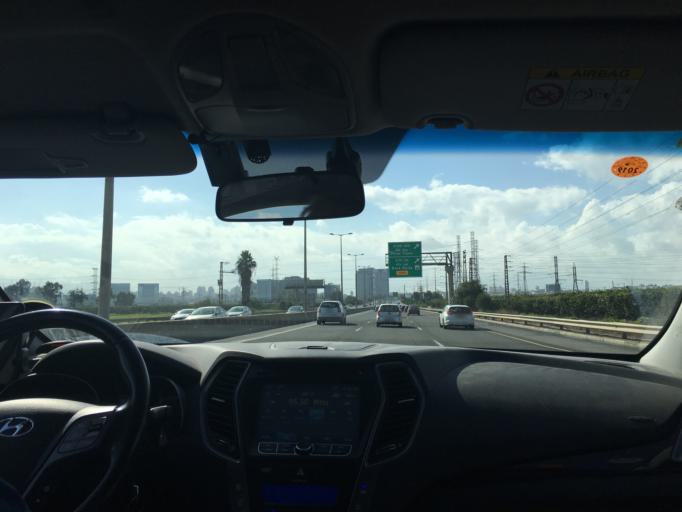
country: IL
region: Tel Aviv
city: Giv`at Shemu'el
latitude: 32.1124
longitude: 34.8504
